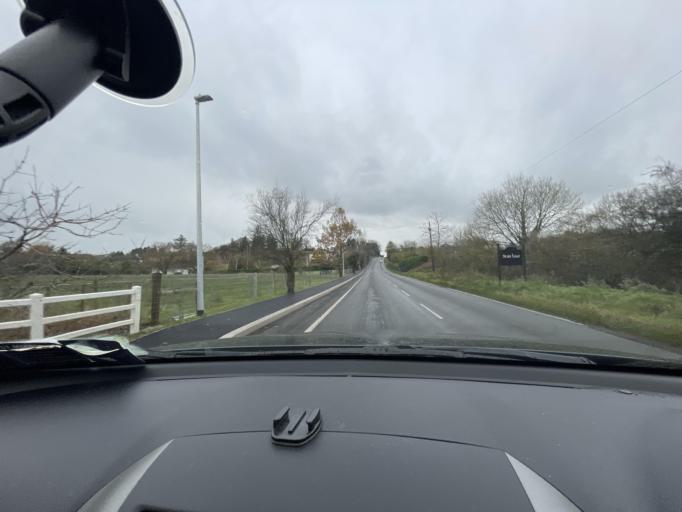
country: IE
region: Ulster
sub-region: An Cabhan
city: Virginia
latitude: 53.8408
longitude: -7.0714
